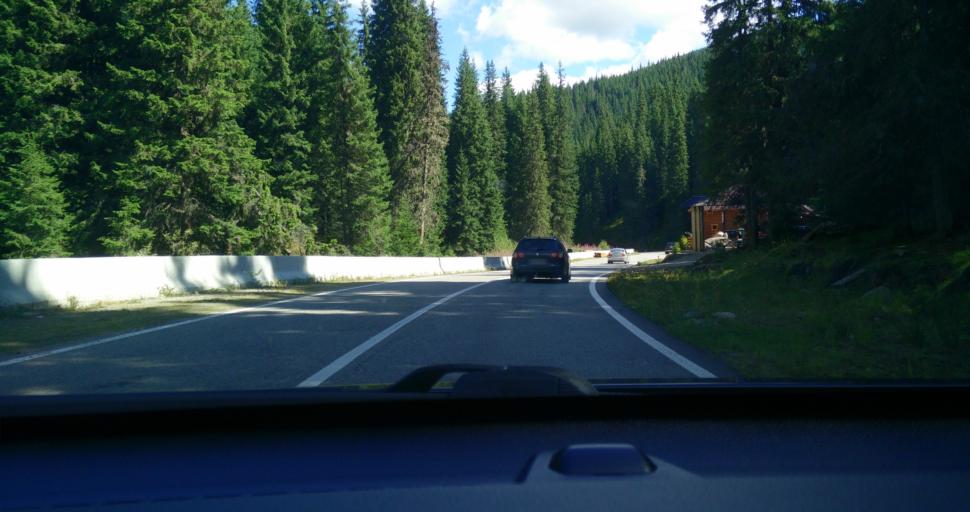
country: RO
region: Hunedoara
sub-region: Oras Petrila
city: Petrila
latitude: 45.5120
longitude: 23.6492
